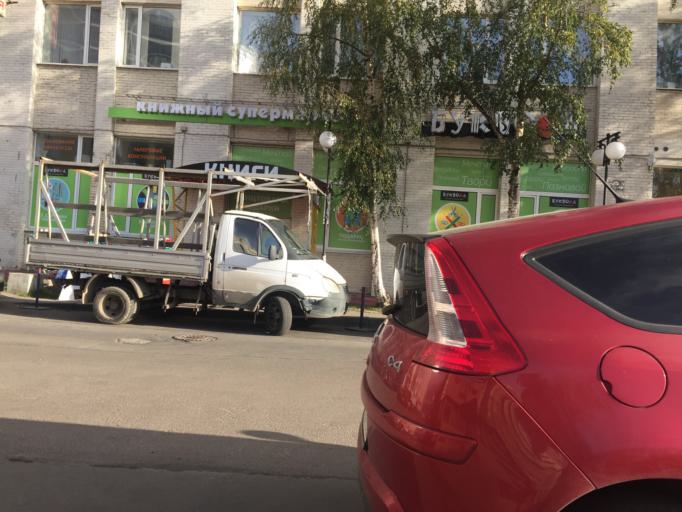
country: RU
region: St.-Petersburg
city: Obukhovo
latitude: 59.8654
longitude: 30.4714
